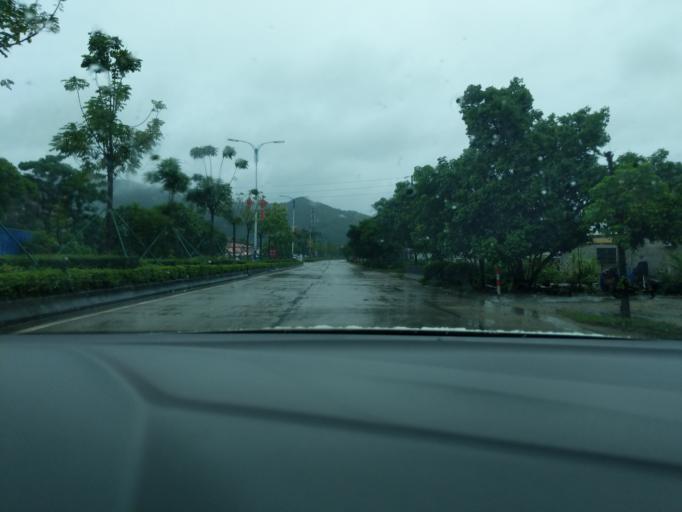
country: CN
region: Guangdong
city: Pingshi
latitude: 22.2126
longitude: 112.3217
